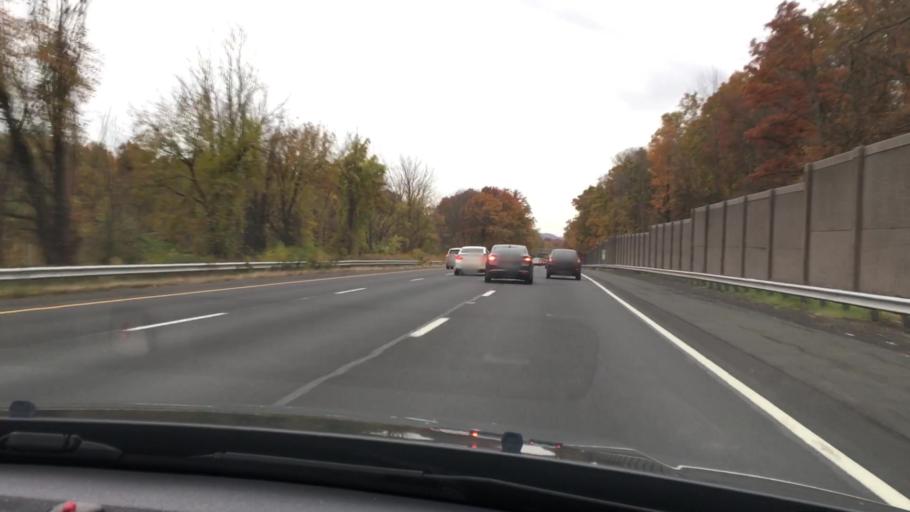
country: US
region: New Jersey
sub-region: Somerset County
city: Bernardsville
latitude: 40.7102
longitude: -74.5582
